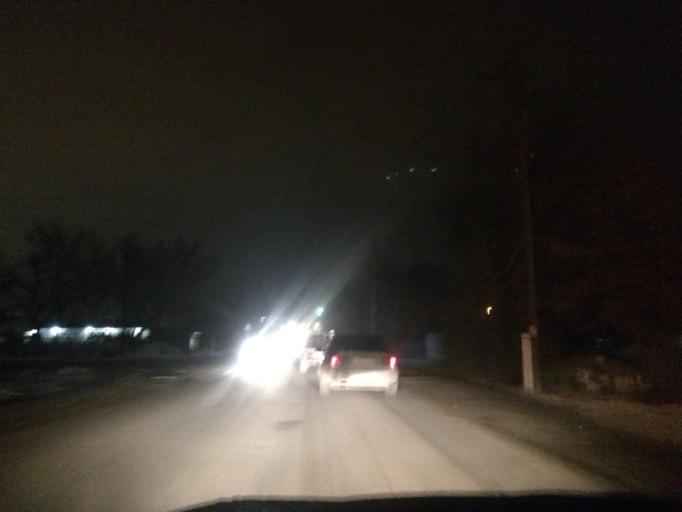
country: KZ
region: Astana Qalasy
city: Astana
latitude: 51.2084
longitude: 71.3808
